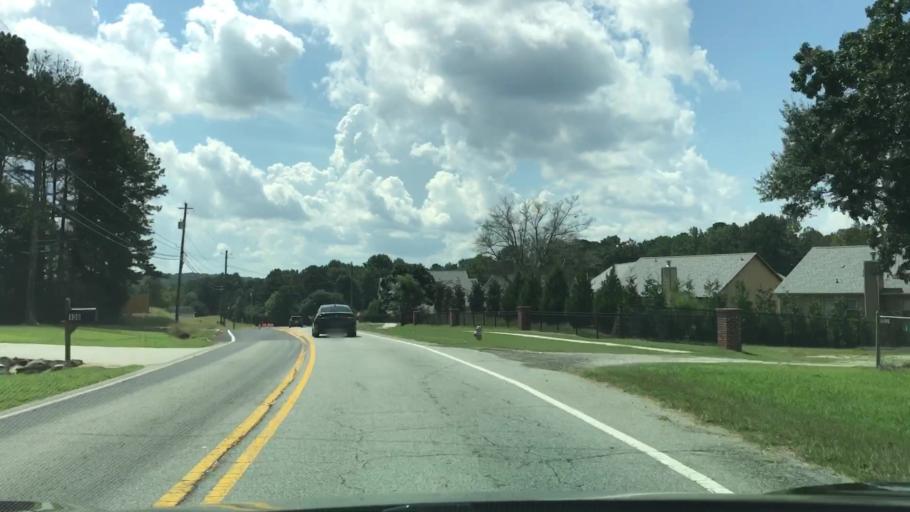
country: US
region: Georgia
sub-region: Gwinnett County
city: Snellville
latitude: 33.9228
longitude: -84.0627
